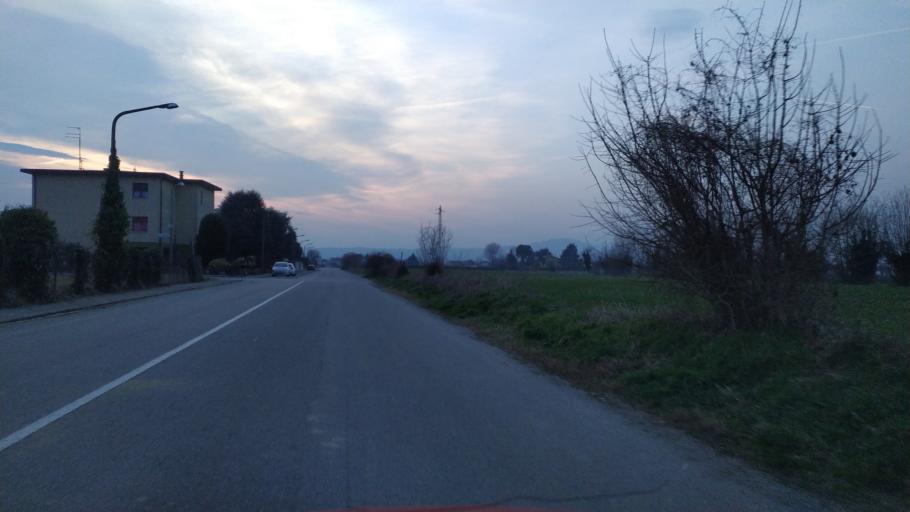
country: IT
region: Veneto
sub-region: Provincia di Vicenza
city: Vicenza
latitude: 45.5785
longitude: 11.5446
